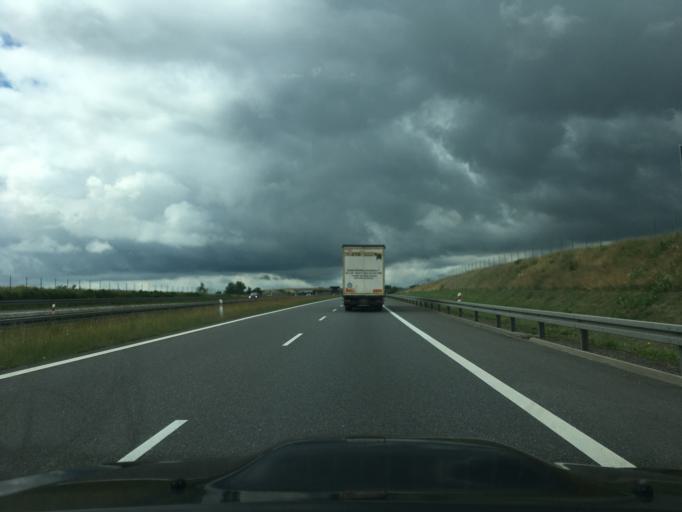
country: PL
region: Lublin Voivodeship
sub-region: Powiat lubelski
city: Jakubowice Murowane
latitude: 51.2918
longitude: 22.6117
